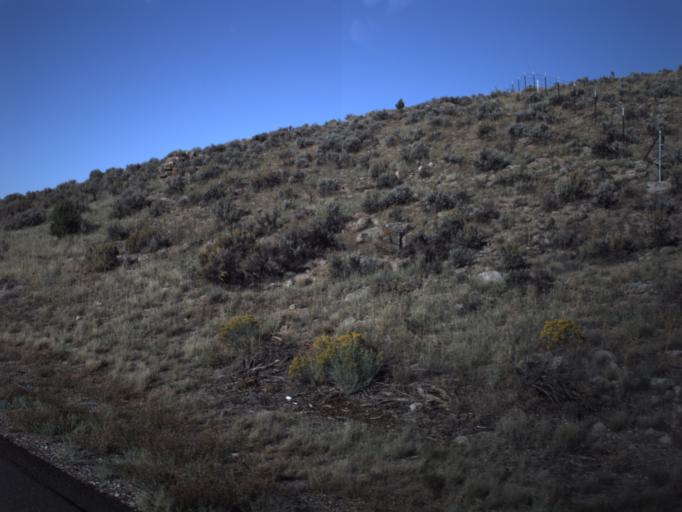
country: US
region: Utah
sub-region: Washington County
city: Enterprise
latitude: 37.7401
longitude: -114.0150
